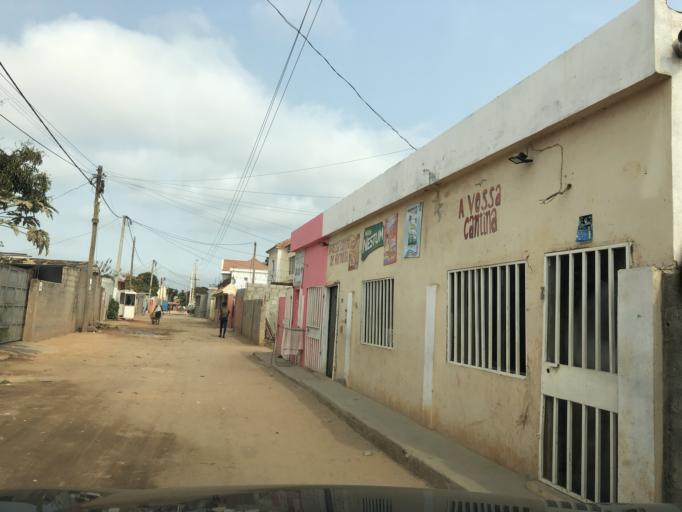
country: AO
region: Luanda
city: Luanda
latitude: -8.9178
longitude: 13.1726
